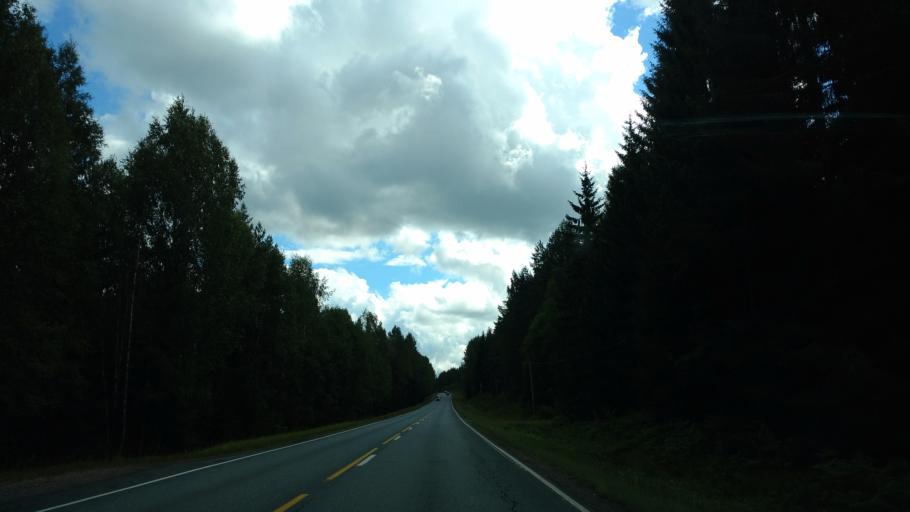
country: FI
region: Uusimaa
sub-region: Helsinki
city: Karjalohja
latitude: 60.2275
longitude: 23.6159
